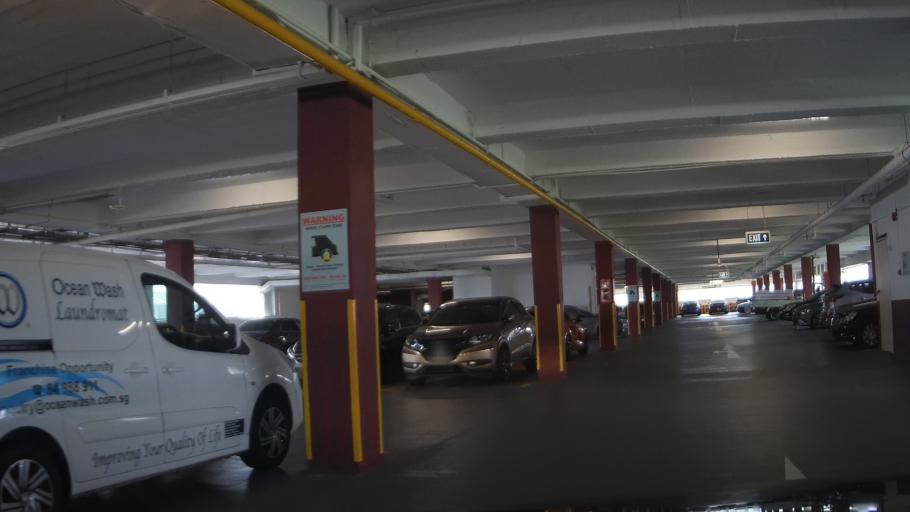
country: SG
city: Singapore
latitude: 1.2229
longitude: 103.8559
